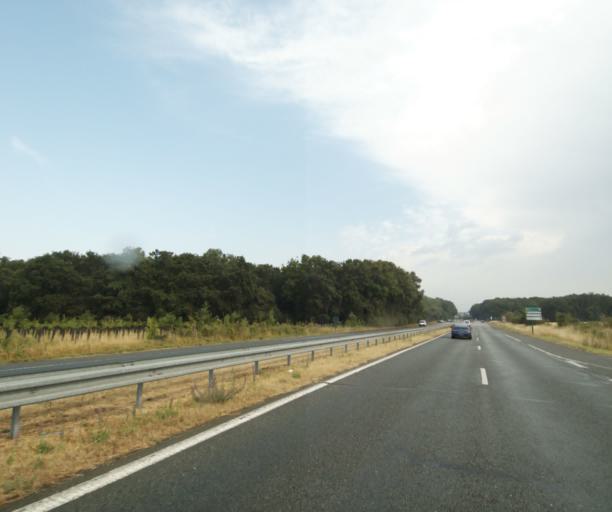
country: FR
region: Ile-de-France
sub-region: Departement du Val-d'Oise
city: Neuville-sur-Oise
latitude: 49.0096
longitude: 2.0742
